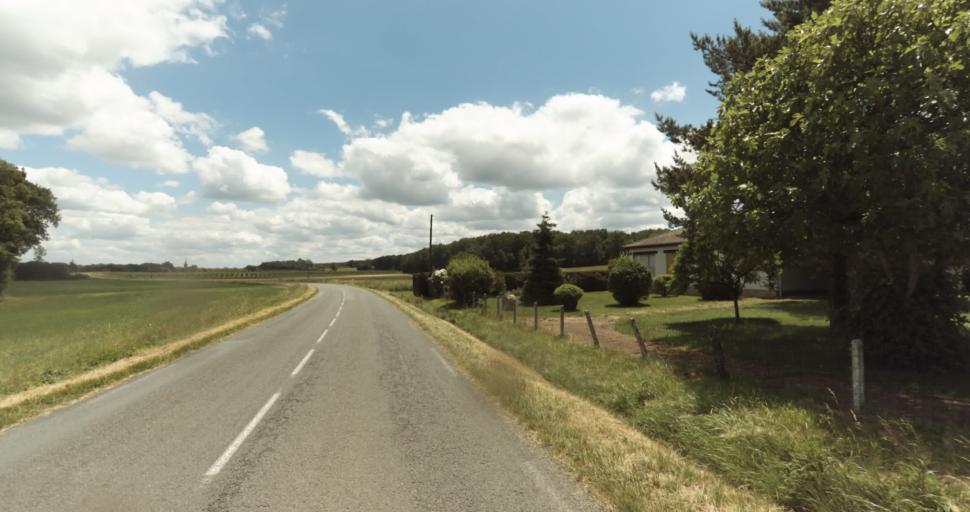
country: FR
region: Aquitaine
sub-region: Departement de la Dordogne
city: Beaumont-du-Perigord
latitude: 44.6972
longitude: 0.8532
